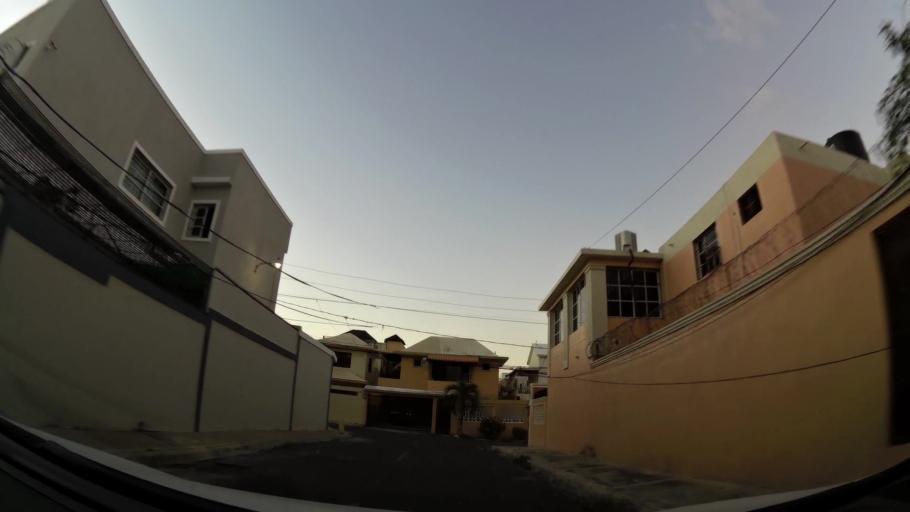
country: DO
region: Santo Domingo
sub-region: Santo Domingo
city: Santo Domingo Este
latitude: 18.4889
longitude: -69.8384
